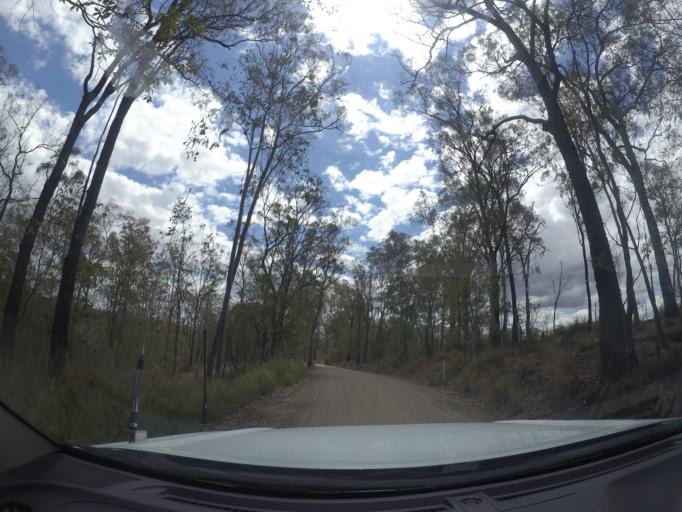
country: AU
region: Queensland
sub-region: Logan
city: Cedar Vale
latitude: -27.8921
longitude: 153.0452
